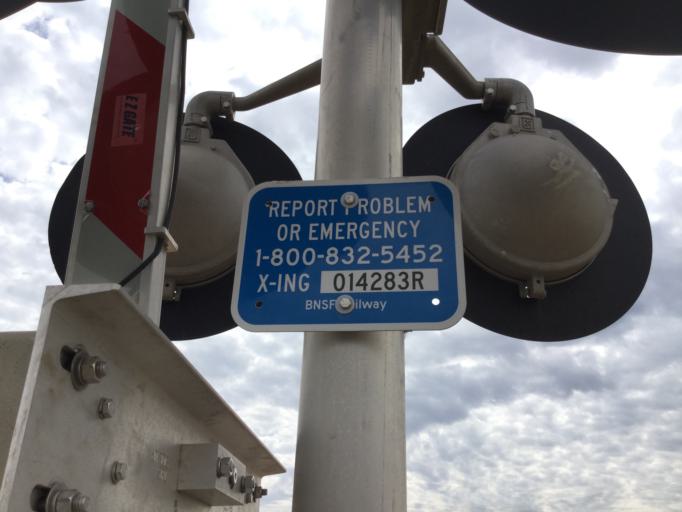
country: US
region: Kansas
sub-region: Barber County
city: Kiowa
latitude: 37.0918
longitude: -98.4085
